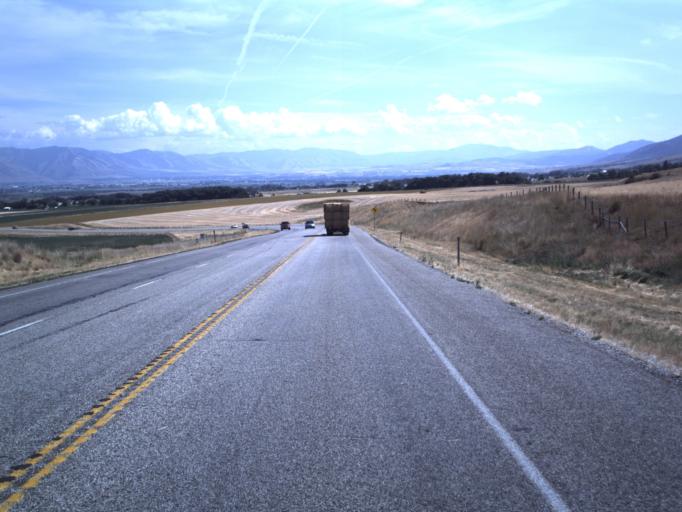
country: US
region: Utah
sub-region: Cache County
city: Mendon
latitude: 41.7593
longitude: -112.0059
